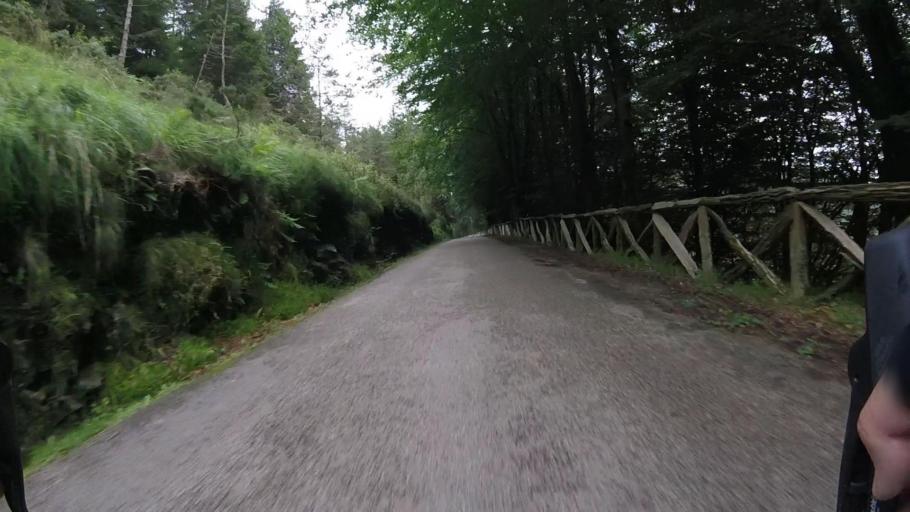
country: ES
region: Navarre
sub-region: Provincia de Navarra
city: Arantza
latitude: 43.2424
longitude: -1.8040
